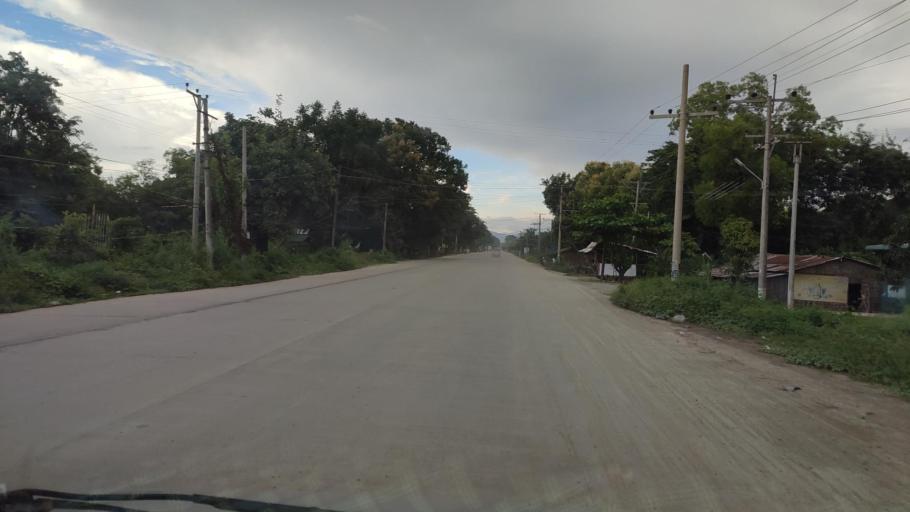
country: MM
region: Bago
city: Taungoo
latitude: 18.9027
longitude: 96.4327
